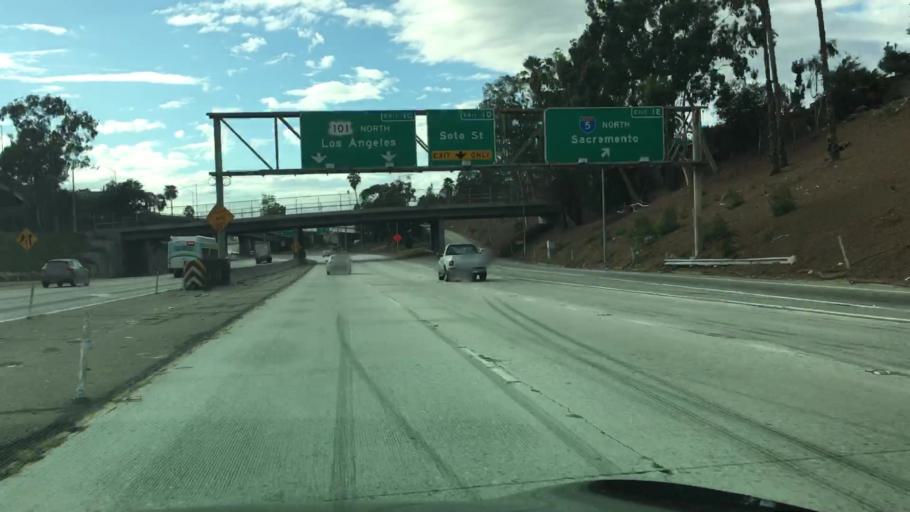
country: US
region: California
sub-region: Los Angeles County
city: Boyle Heights
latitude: 34.0292
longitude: -118.2115
